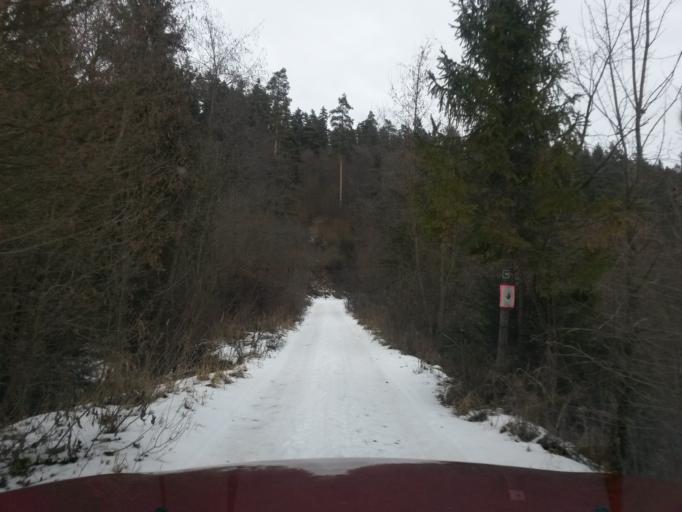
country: SK
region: Kosicky
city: Spisska Nova Ves
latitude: 48.8899
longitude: 20.6064
